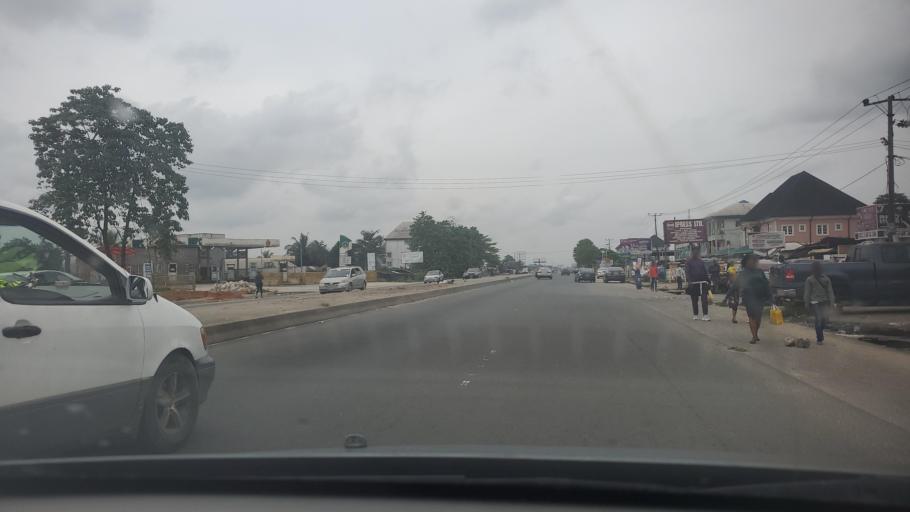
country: NG
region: Rivers
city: Port Harcourt
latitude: 4.8704
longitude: 6.9708
